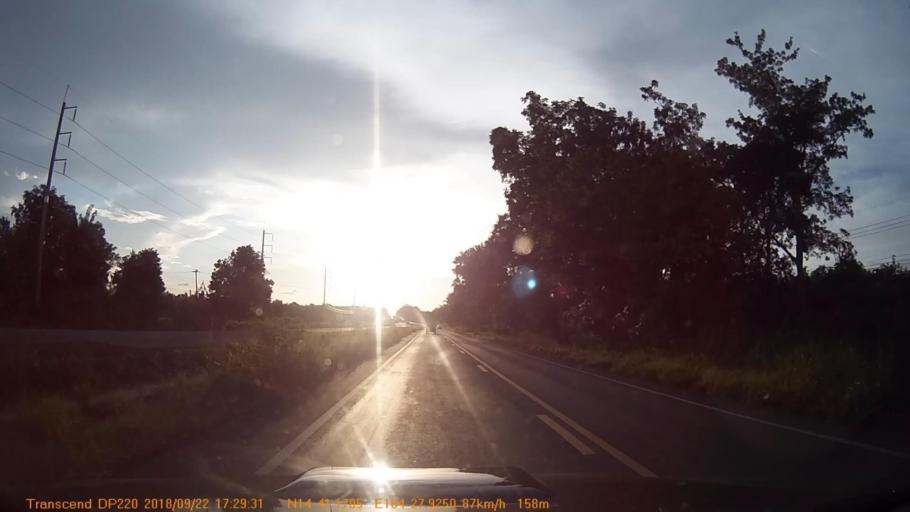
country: TH
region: Sisaket
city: Khun Han
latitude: 14.6862
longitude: 104.4652
